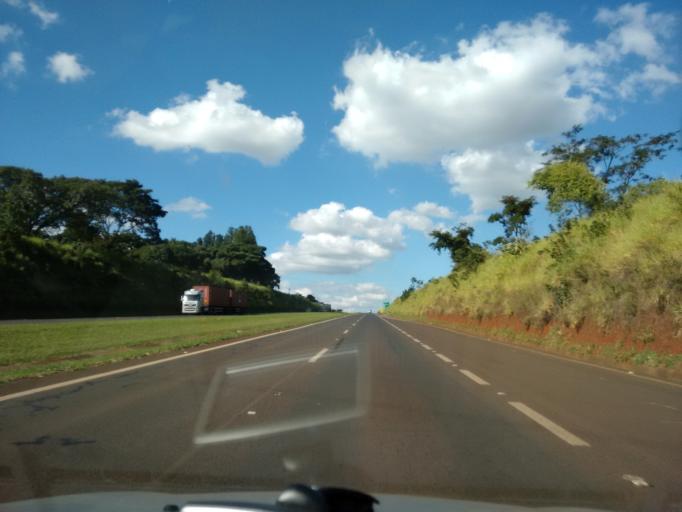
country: BR
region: Sao Paulo
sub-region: Araraquara
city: Araraquara
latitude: -21.8146
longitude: -48.1660
